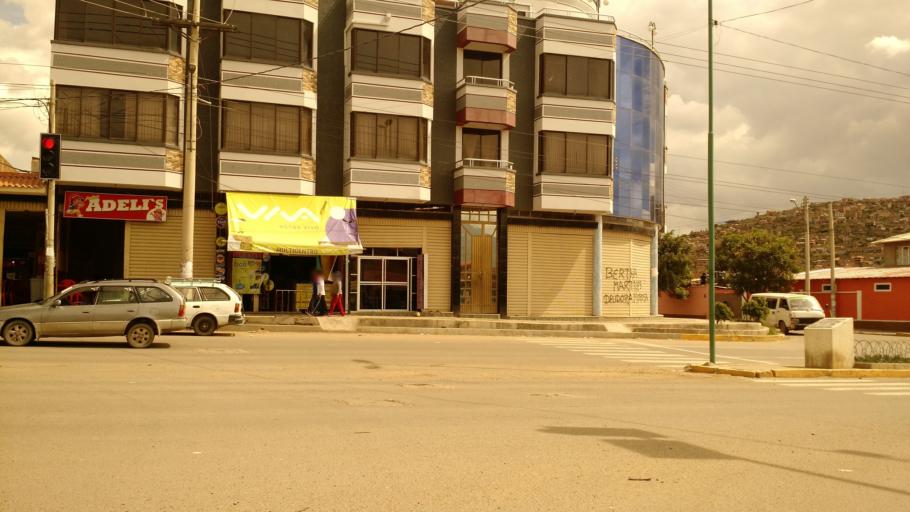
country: BO
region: Cochabamba
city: Cochabamba
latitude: -17.4230
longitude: -66.1244
